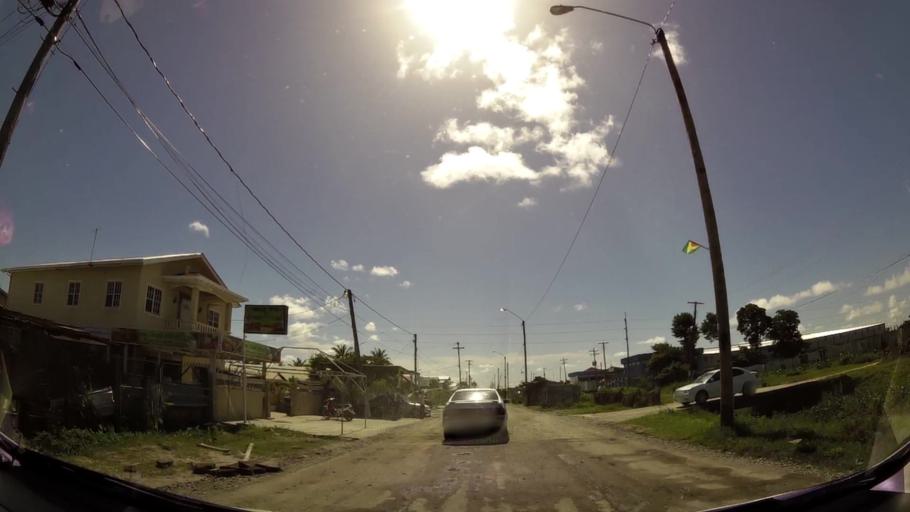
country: GY
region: Demerara-Mahaica
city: Georgetown
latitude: 6.8094
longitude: -58.1240
